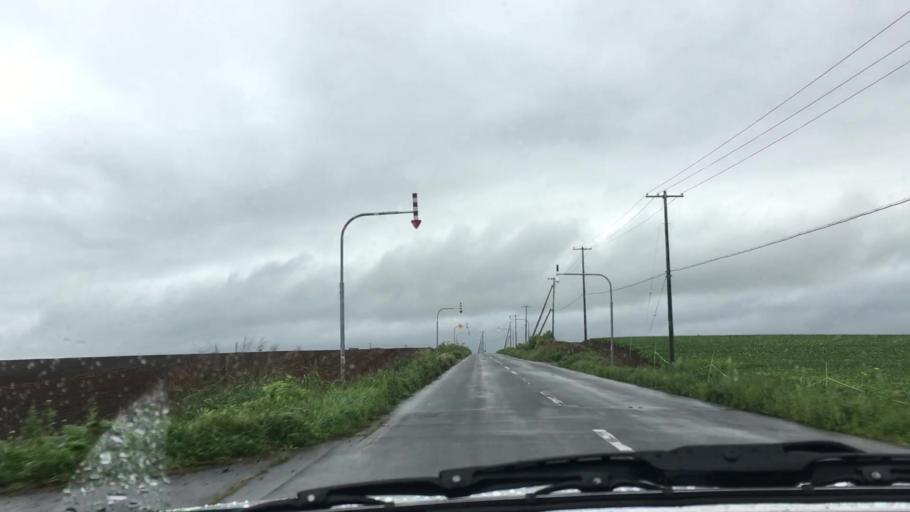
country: JP
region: Hokkaido
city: Niseko Town
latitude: 42.6813
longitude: 140.8032
